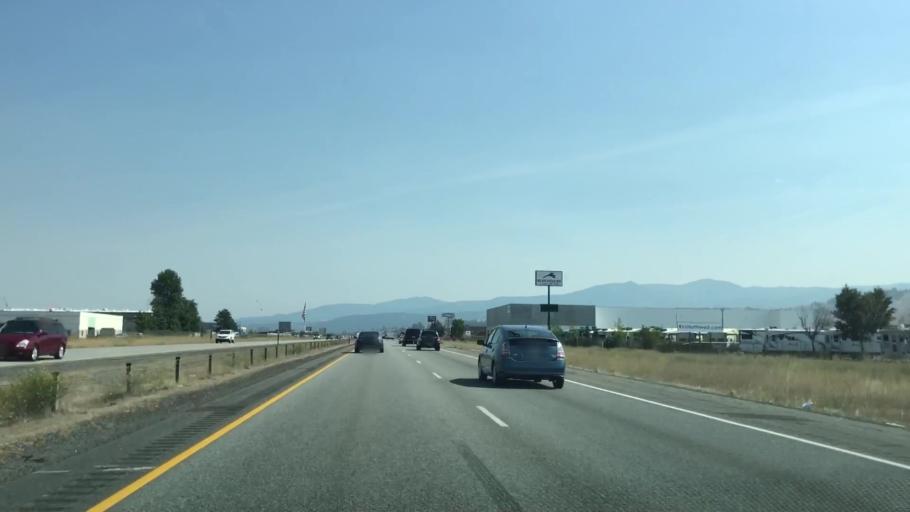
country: US
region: Washington
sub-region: Spokane County
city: Liberty Lake
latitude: 47.6643
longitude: -117.1502
